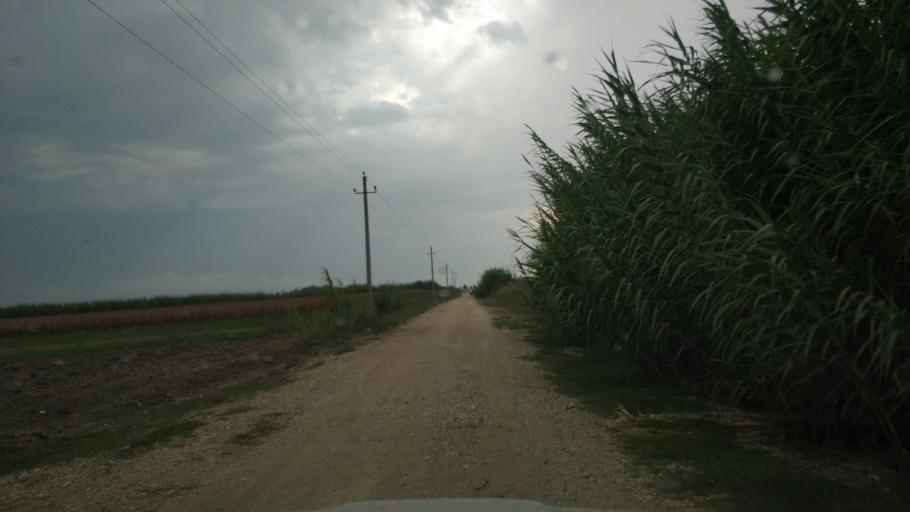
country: AL
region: Fier
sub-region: Rrethi i Fierit
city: Topoje
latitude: 40.7144
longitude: 19.4519
